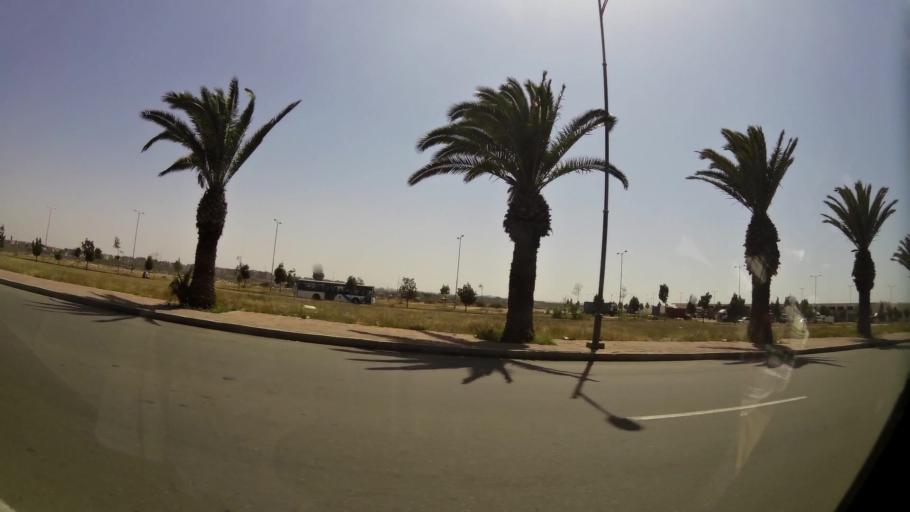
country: MA
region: Souss-Massa-Draa
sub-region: Inezgane-Ait Mellou
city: Inezgane
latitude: 30.3569
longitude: -9.5174
